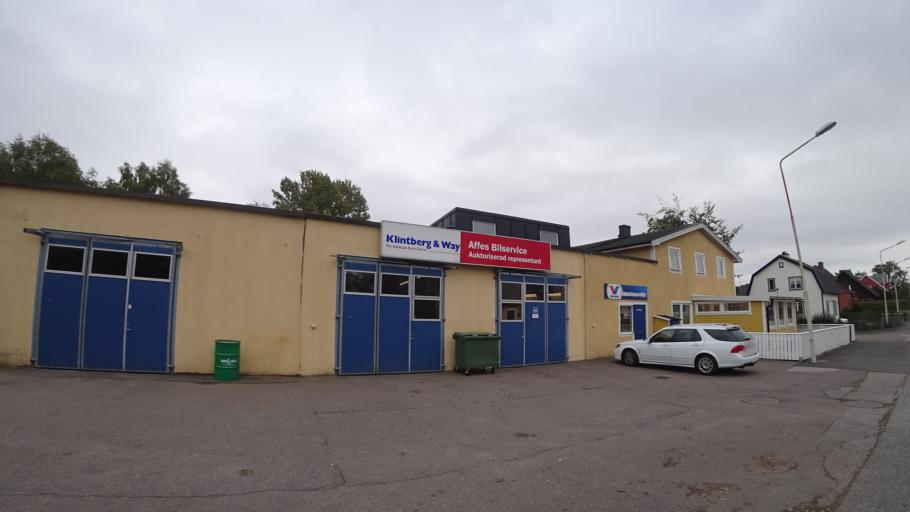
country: SE
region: Skane
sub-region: Kavlinge Kommun
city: Kaevlinge
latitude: 55.7814
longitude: 13.1078
